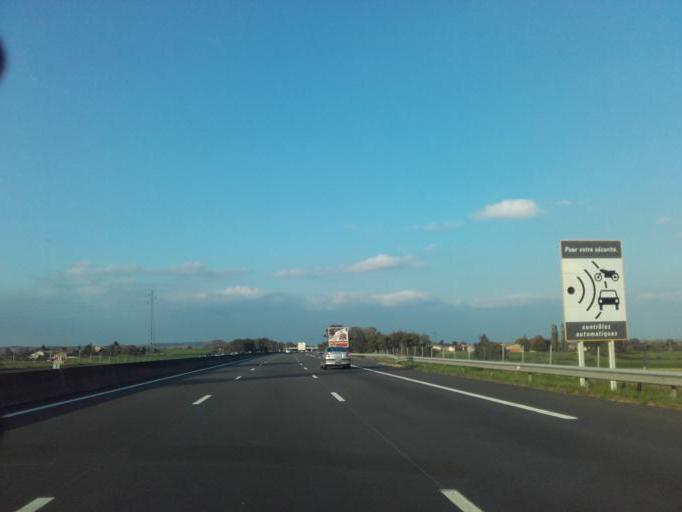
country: FR
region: Rhone-Alpes
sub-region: Departement de l'Ain
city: Pont-de-Vaux
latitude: 46.4587
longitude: 4.8758
